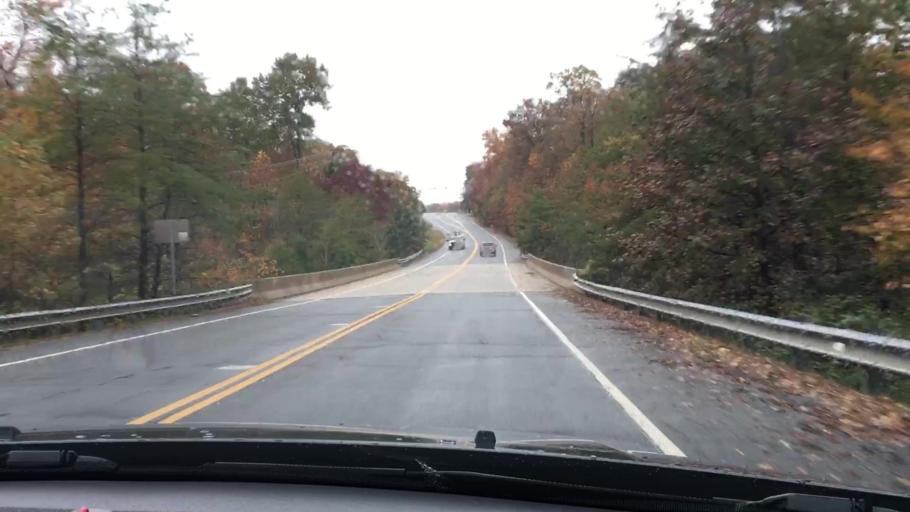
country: US
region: Virginia
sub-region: Fairfax County
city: Burke
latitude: 38.7481
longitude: -77.2820
